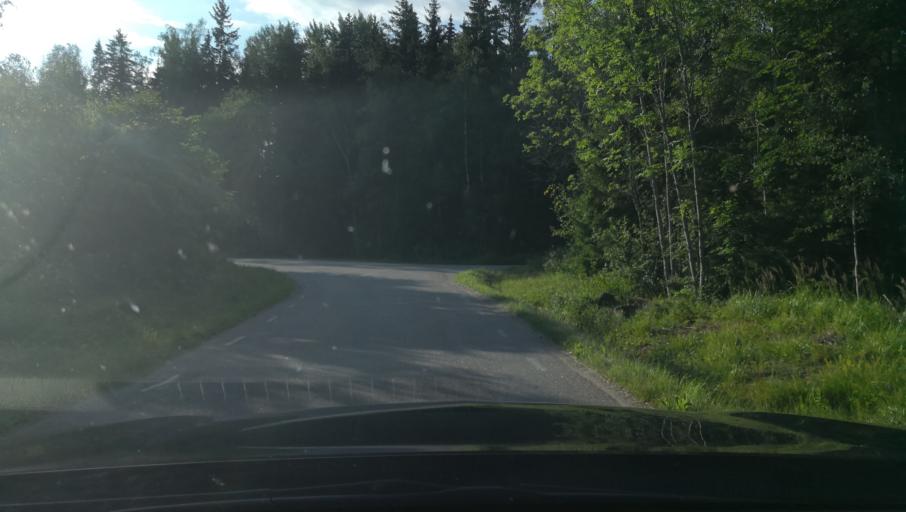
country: SE
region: Uppsala
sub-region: Osthammars Kommun
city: Osterbybruk
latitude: 60.0211
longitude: 17.9170
